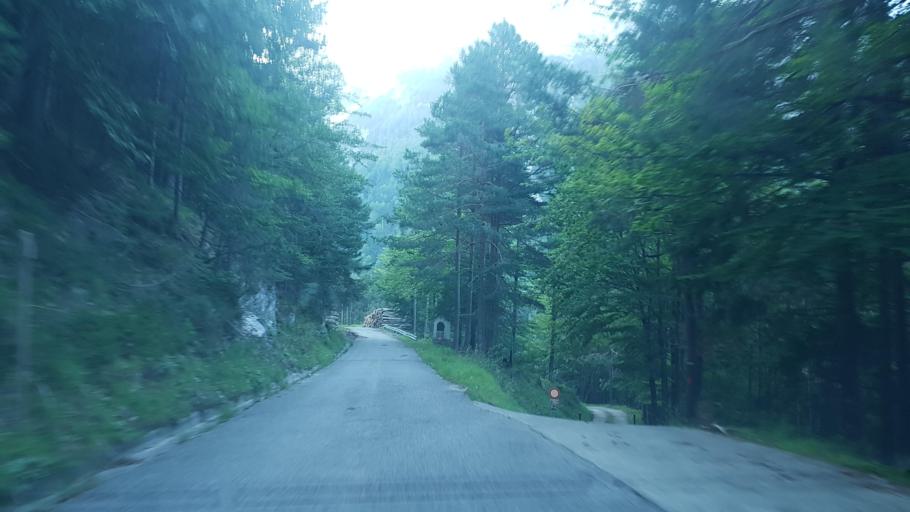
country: IT
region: Friuli Venezia Giulia
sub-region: Provincia di Udine
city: Malborghetto
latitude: 46.4577
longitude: 13.4083
